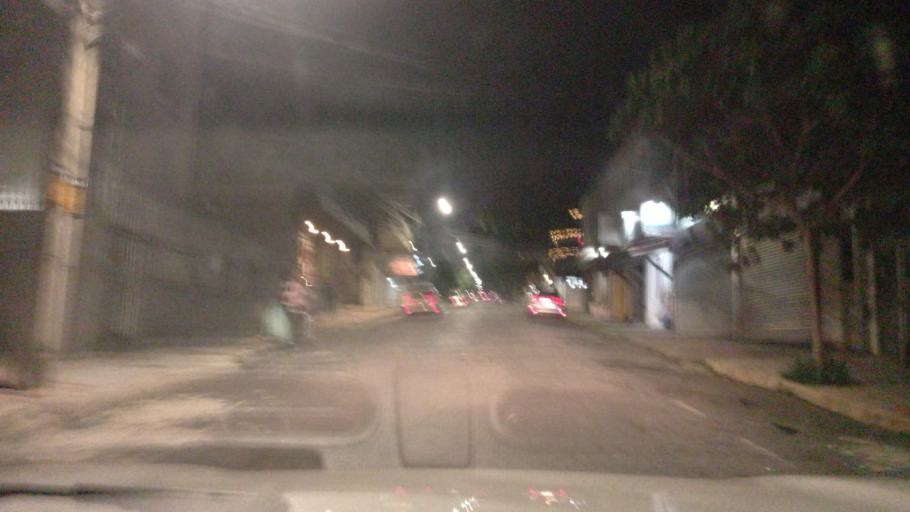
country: BR
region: Minas Gerais
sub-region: Belo Horizonte
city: Belo Horizonte
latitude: -19.8889
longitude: -43.9247
